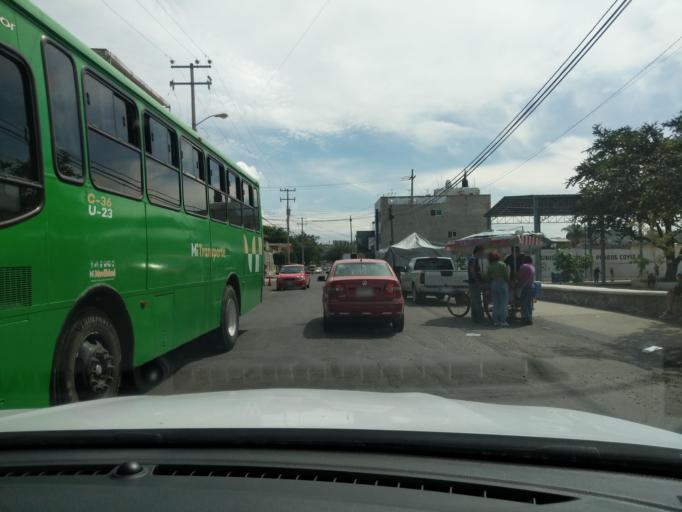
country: MX
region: Jalisco
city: Tonala
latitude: 20.6506
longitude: -103.2273
